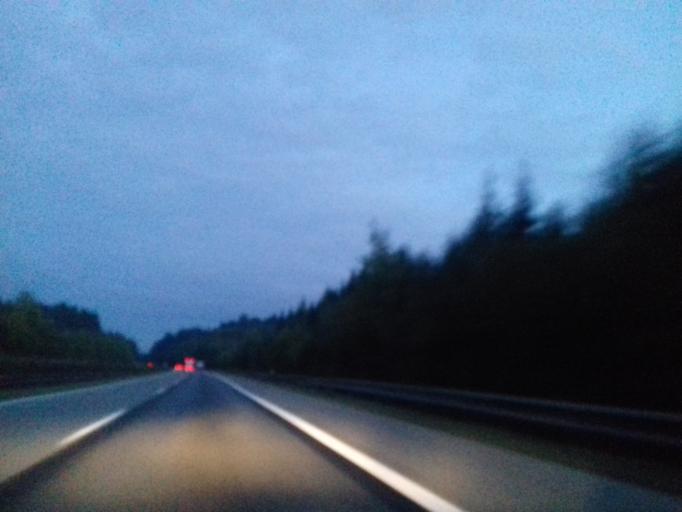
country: CZ
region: Vysocina
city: Vilemov
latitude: 49.5180
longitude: 15.3957
